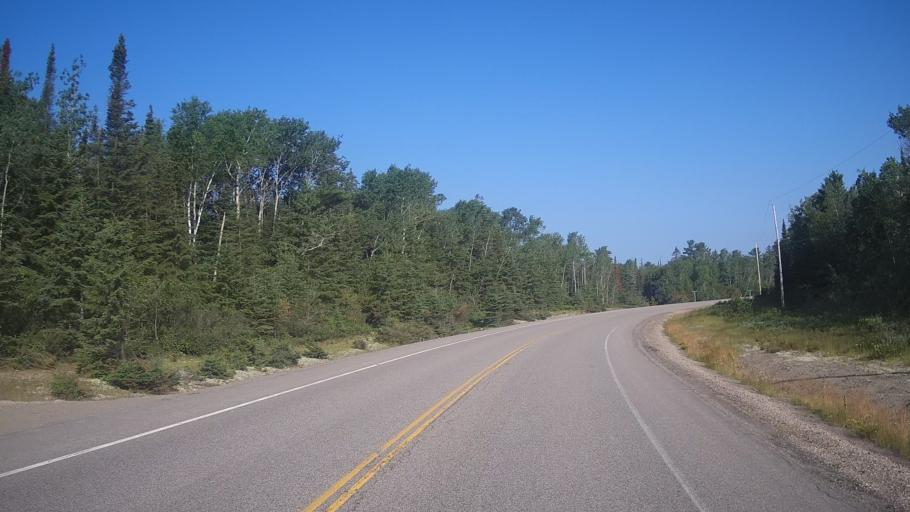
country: CA
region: Ontario
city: Rayside-Balfour
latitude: 46.7319
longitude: -81.5889
